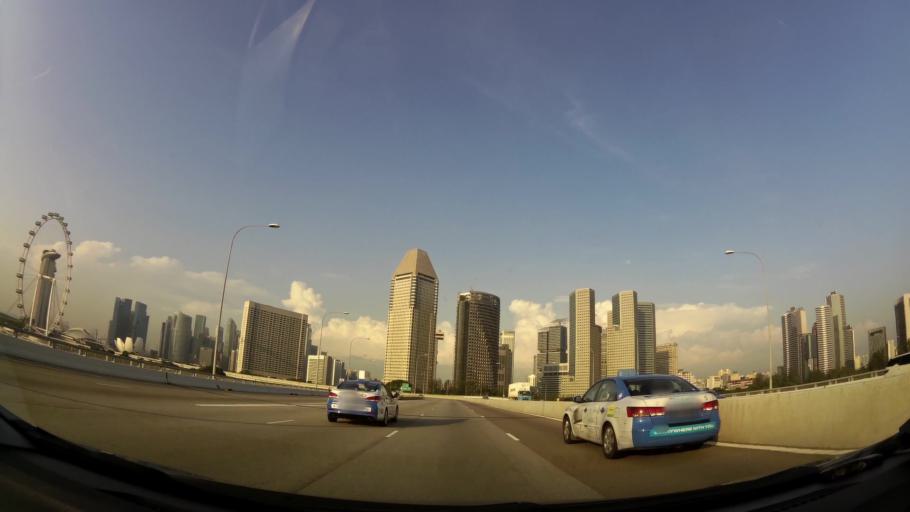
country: SG
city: Singapore
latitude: 1.2941
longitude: 103.8651
